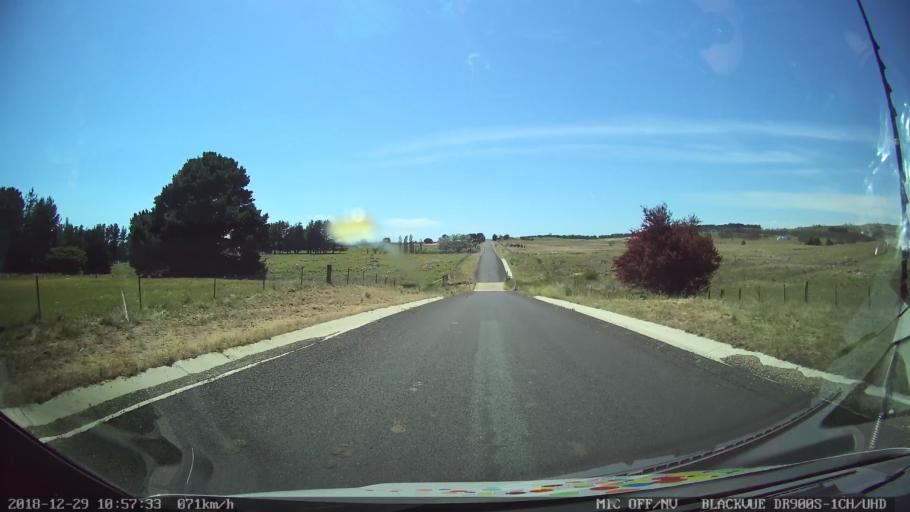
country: AU
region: New South Wales
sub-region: Palerang
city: Bungendore
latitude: -35.1366
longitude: 149.5496
